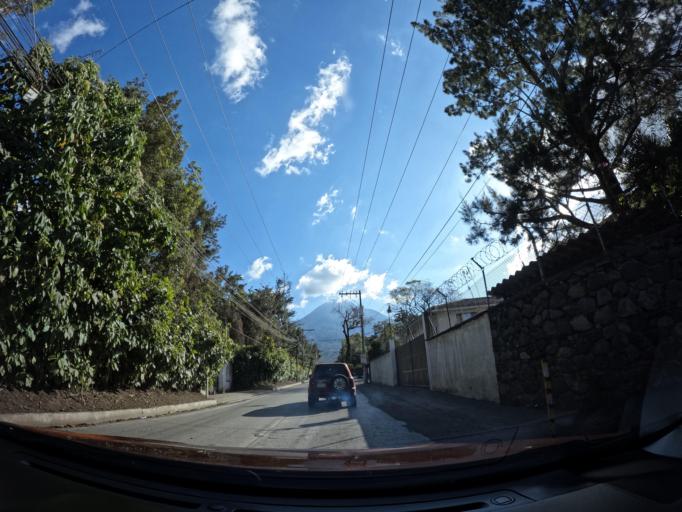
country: GT
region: Sacatepequez
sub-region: Municipio de Santa Maria de Jesus
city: Santa Maria de Jesus
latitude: 14.5391
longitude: -90.7295
